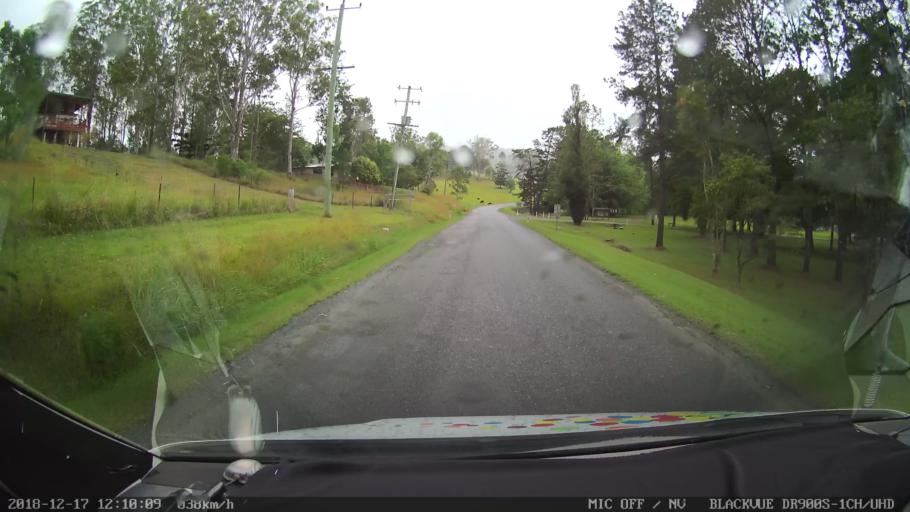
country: AU
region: New South Wales
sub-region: Kyogle
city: Kyogle
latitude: -28.4688
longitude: 152.5481
